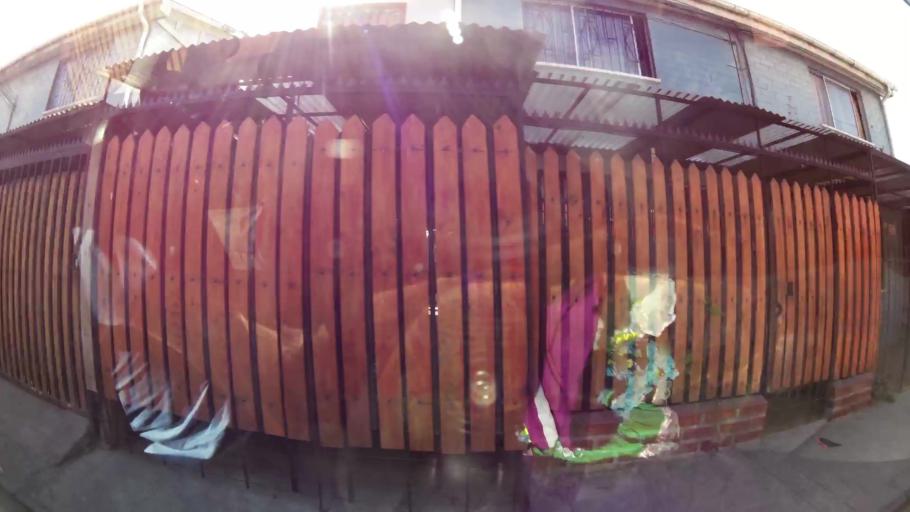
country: CL
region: Santiago Metropolitan
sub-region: Provincia de Santiago
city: Lo Prado
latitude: -33.3606
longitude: -70.7515
